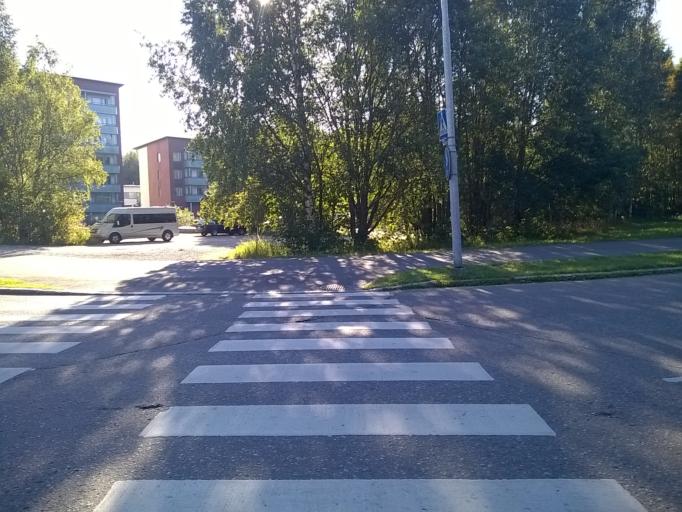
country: FI
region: Pirkanmaa
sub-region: Tampere
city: Tampere
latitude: 61.4484
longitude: 23.8387
